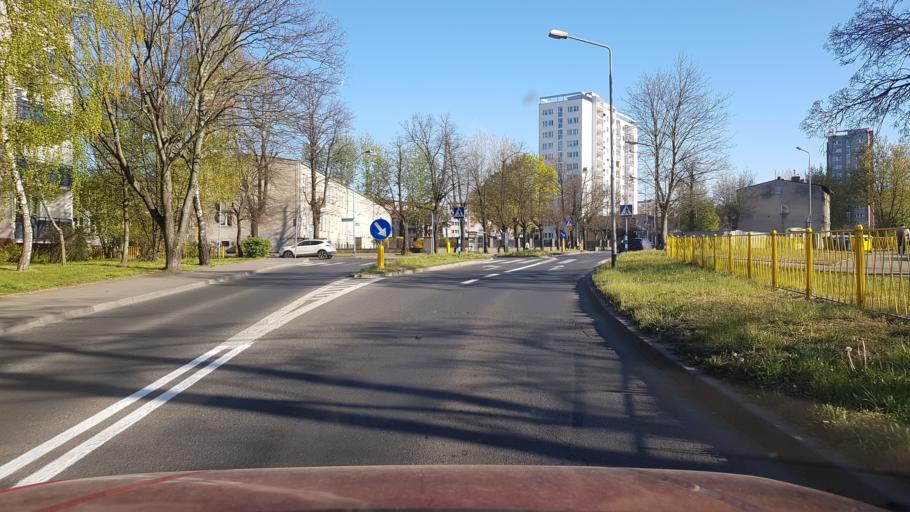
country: PL
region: West Pomeranian Voivodeship
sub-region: Szczecin
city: Szczecin
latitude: 53.3823
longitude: 14.6350
